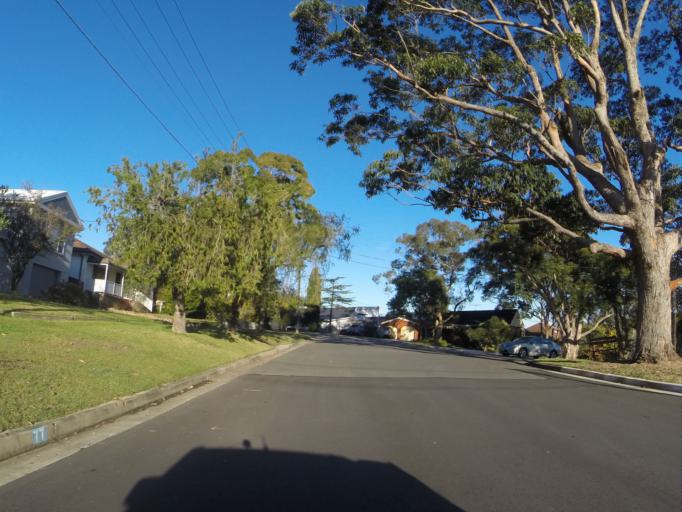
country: AU
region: New South Wales
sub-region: Sutherland Shire
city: Loftus
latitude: -34.0412
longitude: 151.0432
